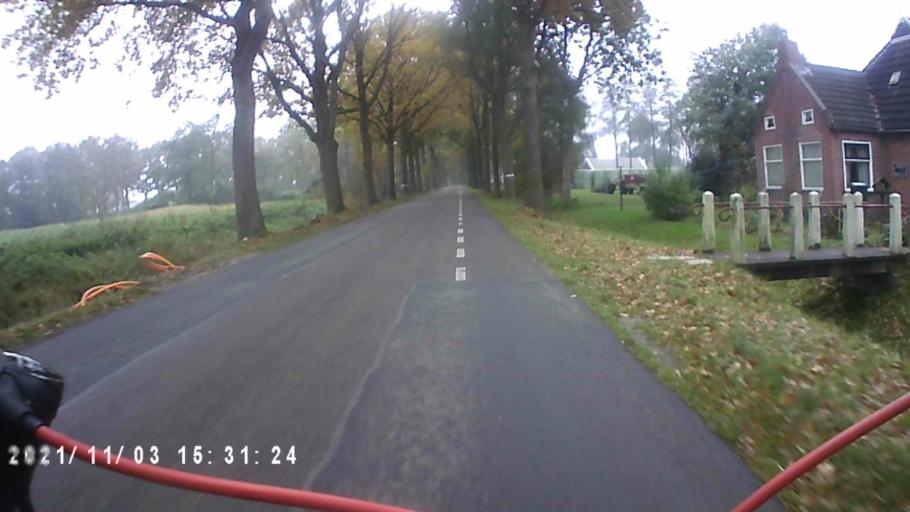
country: NL
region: Groningen
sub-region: Gemeente Leek
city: Leek
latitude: 53.1296
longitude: 6.3689
